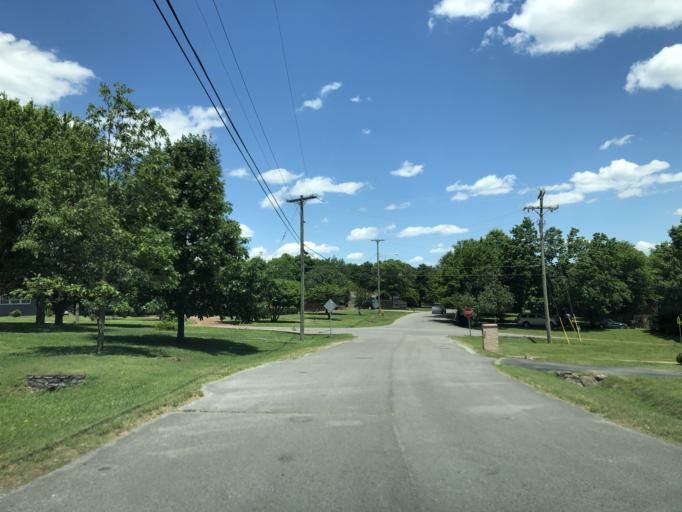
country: US
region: Tennessee
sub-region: Davidson County
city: Nashville
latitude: 36.1855
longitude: -86.7184
